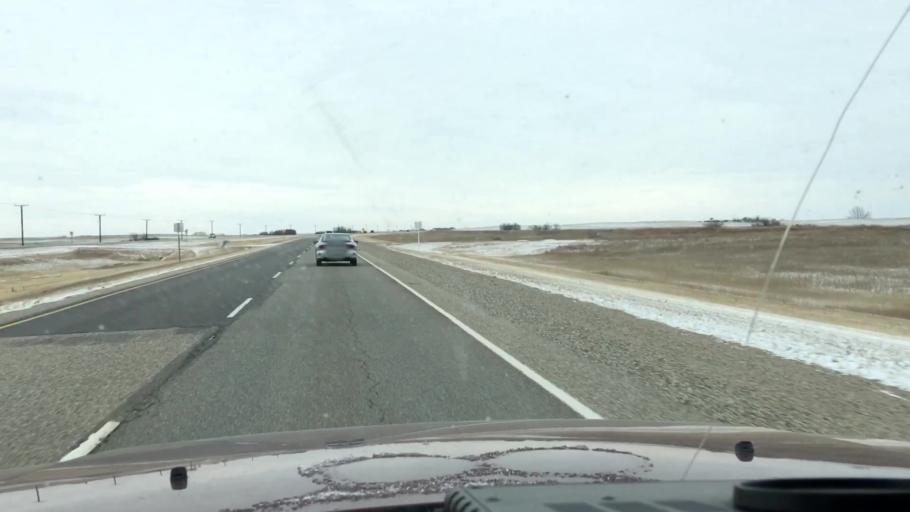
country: CA
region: Saskatchewan
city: Watrous
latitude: 51.4401
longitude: -106.2085
